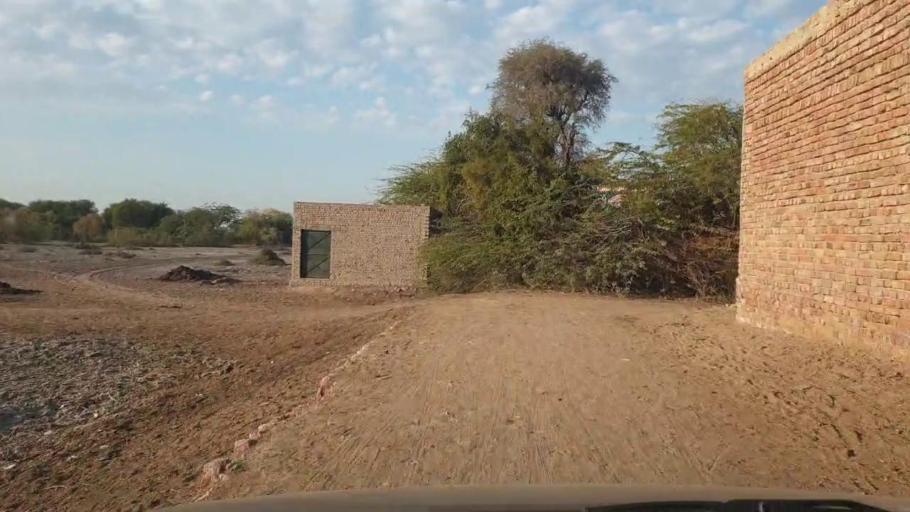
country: PK
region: Sindh
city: Sakrand
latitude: 26.0286
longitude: 68.3894
